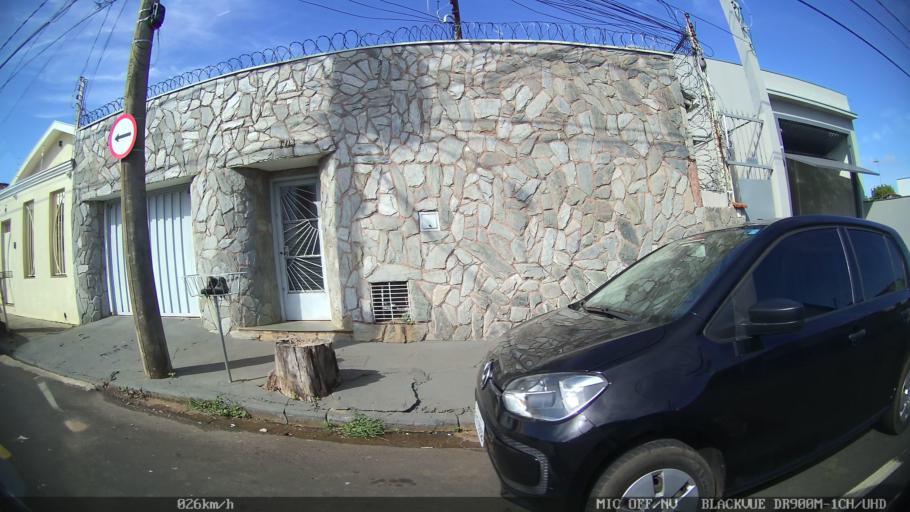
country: BR
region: Sao Paulo
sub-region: Franca
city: Franca
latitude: -20.5362
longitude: -47.4173
